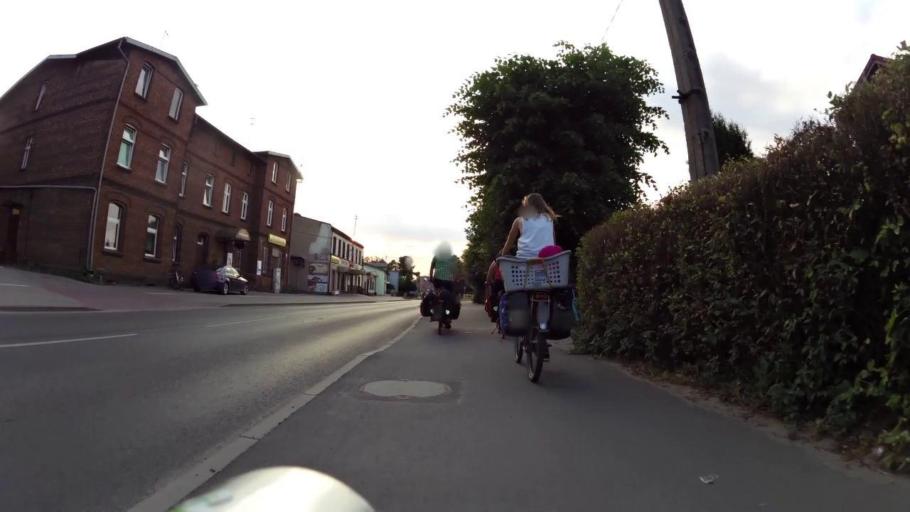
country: PL
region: Kujawsko-Pomorskie
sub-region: Powiat bydgoski
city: Dabrowa Chelminska
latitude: 53.1762
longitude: 18.3026
